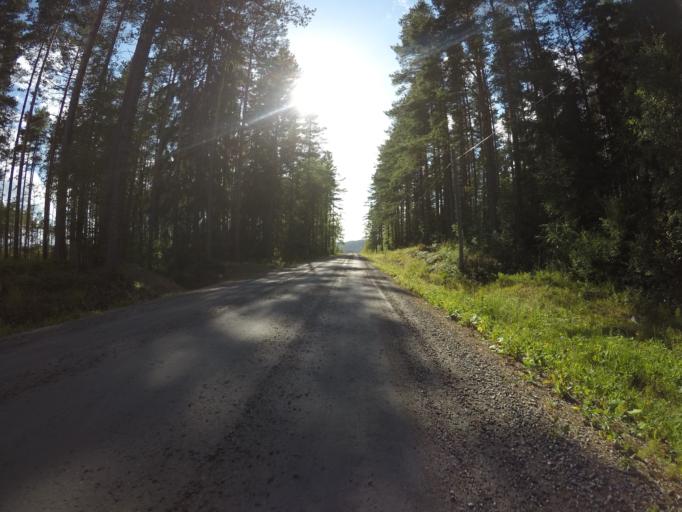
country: SE
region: OErebro
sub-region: Hallefors Kommun
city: Haellefors
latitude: 59.9032
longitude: 14.5776
